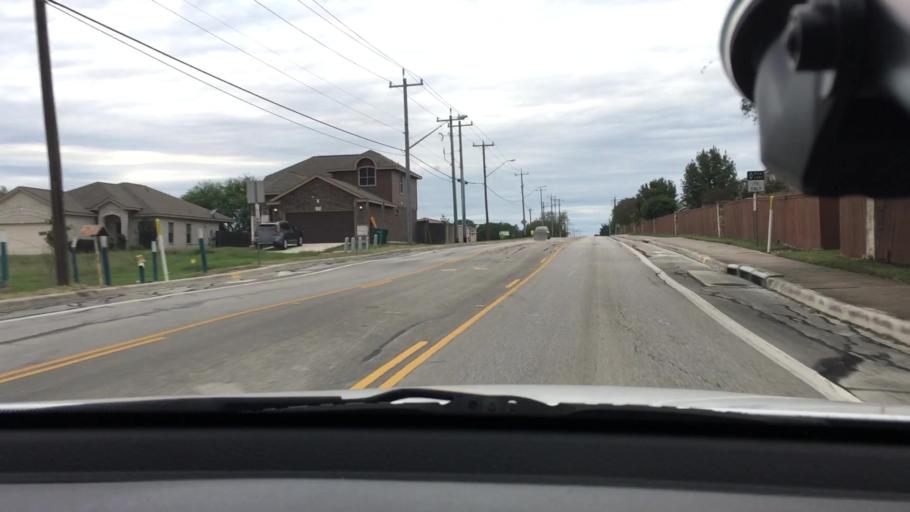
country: US
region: Texas
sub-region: Bexar County
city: Converse
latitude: 29.5288
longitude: -98.3099
